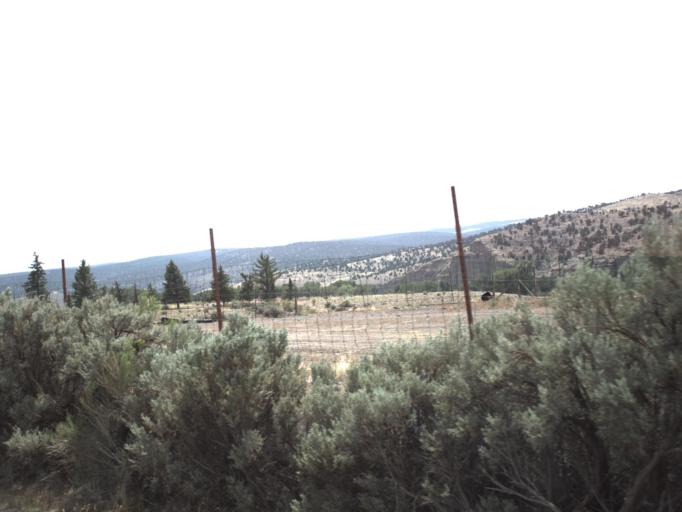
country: US
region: Utah
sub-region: Piute County
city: Junction
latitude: 38.0994
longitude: -111.9838
